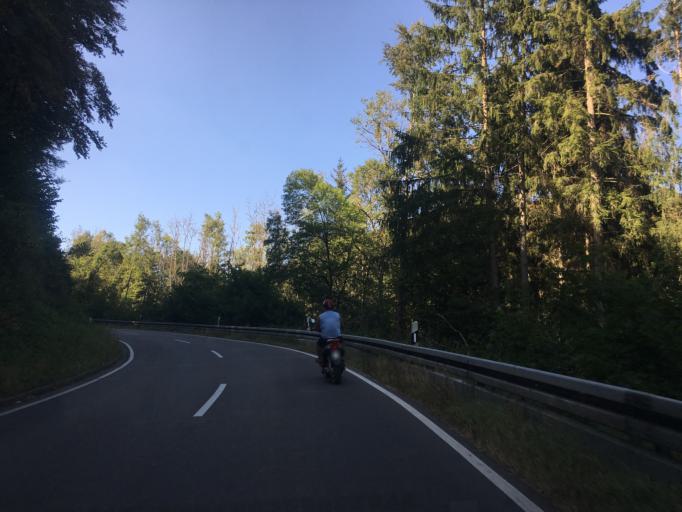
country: DE
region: Baden-Wuerttemberg
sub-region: Tuebingen Region
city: Hayingen
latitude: 48.2933
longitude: 9.4857
